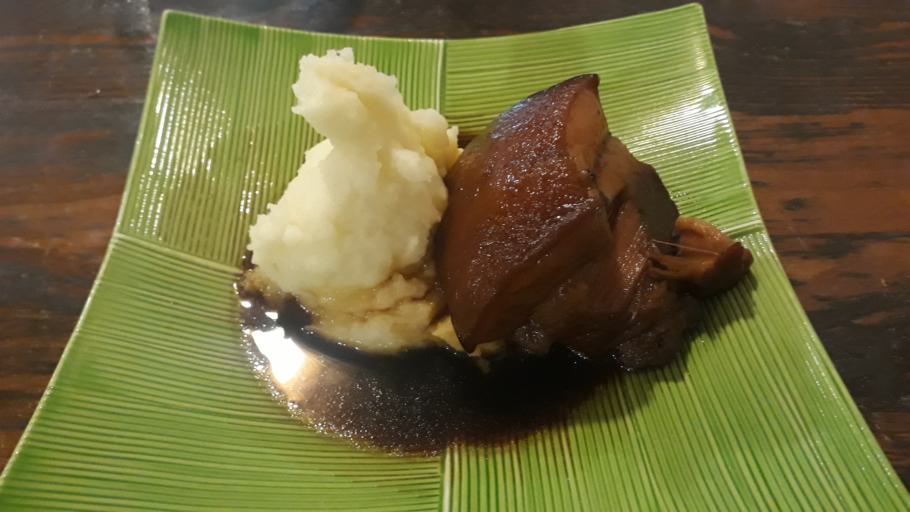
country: JP
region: Okinawa
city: Naha-shi
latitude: 26.2278
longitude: 127.3031
